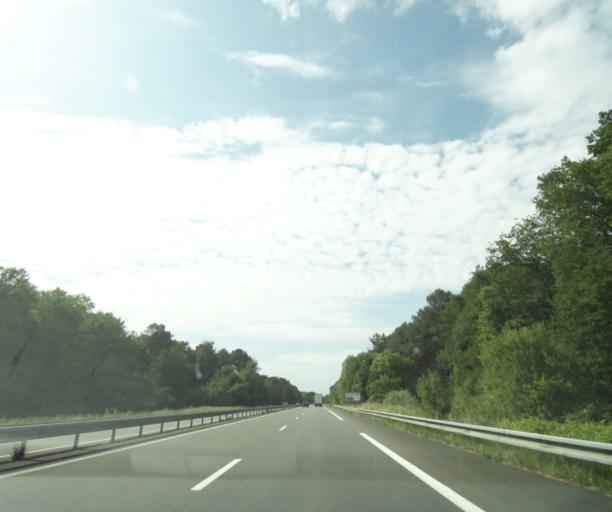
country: FR
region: Pays de la Loire
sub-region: Departement de Maine-et-Loire
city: Baune
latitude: 47.5153
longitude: -0.2999
